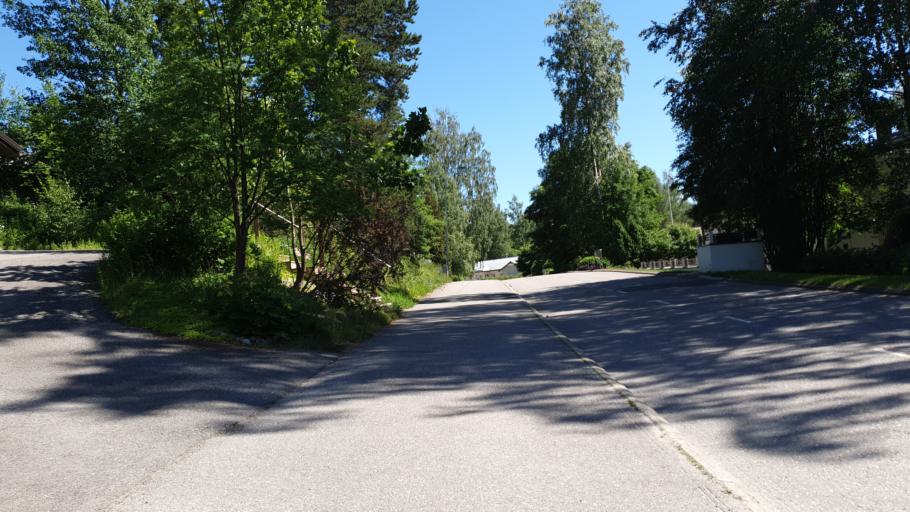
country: FI
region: Uusimaa
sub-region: Helsinki
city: Kilo
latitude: 60.2694
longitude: 24.8311
